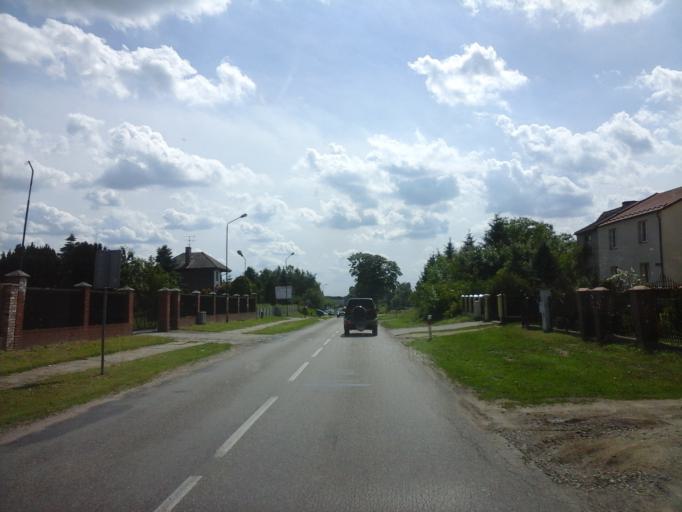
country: PL
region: West Pomeranian Voivodeship
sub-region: Powiat swidwinski
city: Swidwin
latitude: 53.7641
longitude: 15.7527
